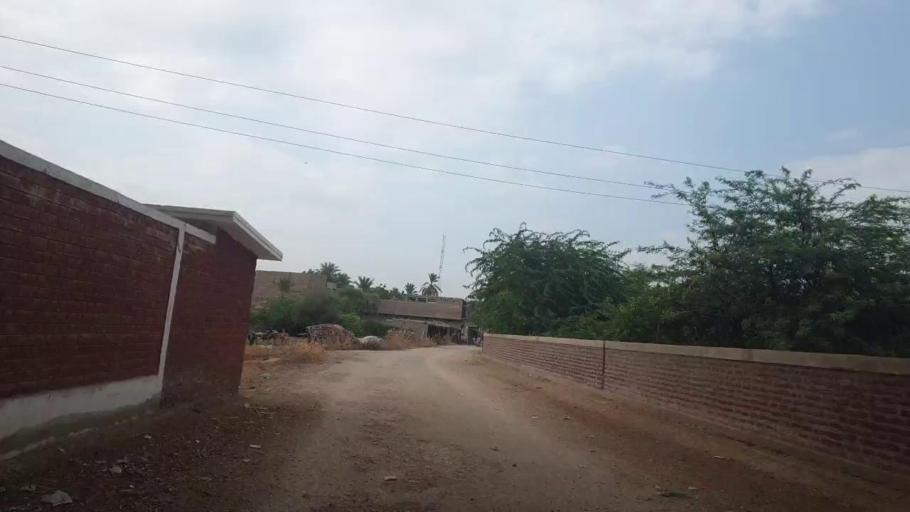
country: PK
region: Sindh
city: Sukkur
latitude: 27.6334
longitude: 68.7929
